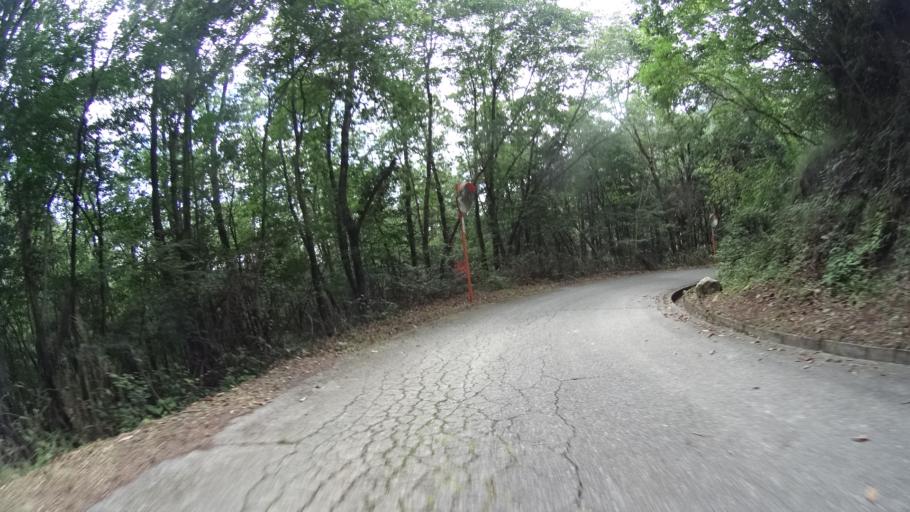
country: JP
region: Yamanashi
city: Nirasaki
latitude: 35.8027
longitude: 138.5273
